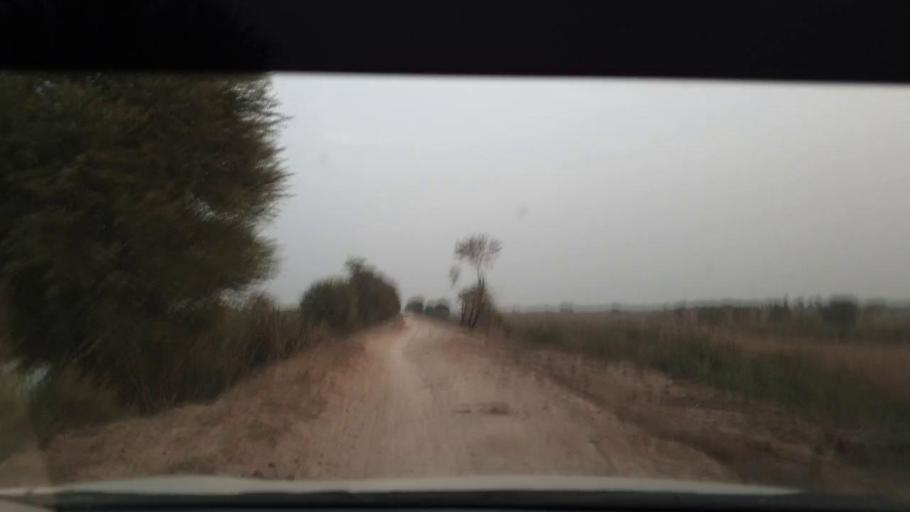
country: PK
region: Sindh
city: Berani
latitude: 25.8604
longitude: 68.7762
